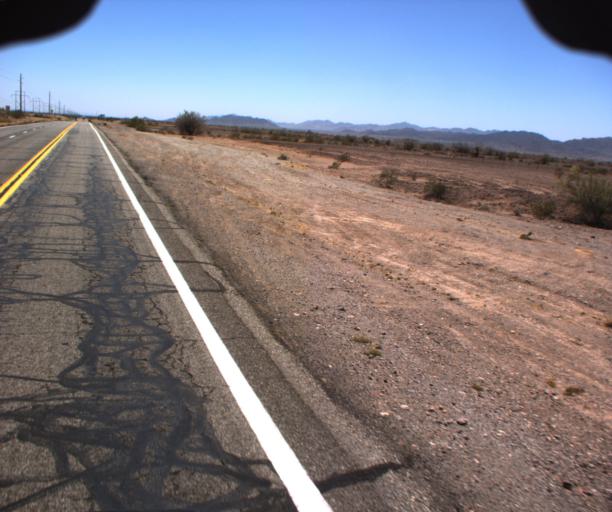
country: US
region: Arizona
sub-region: La Paz County
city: Quartzsite
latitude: 33.7704
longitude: -114.2170
